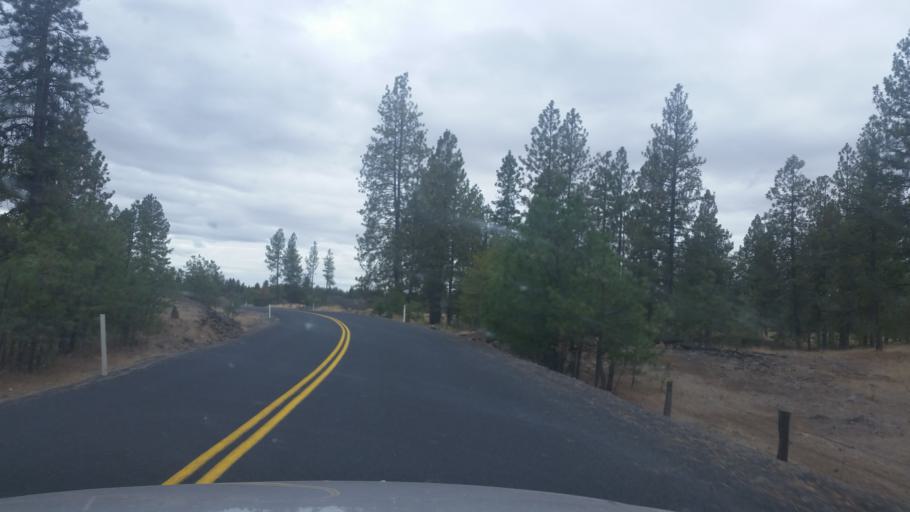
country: US
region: Washington
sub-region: Spokane County
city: Medical Lake
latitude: 47.5168
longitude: -117.7517
